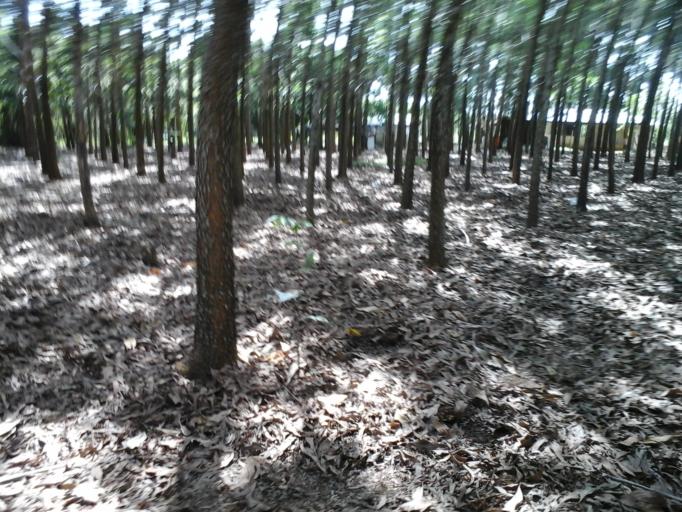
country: CO
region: Cundinamarca
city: Tibacuy
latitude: 4.2218
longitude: -72.4713
